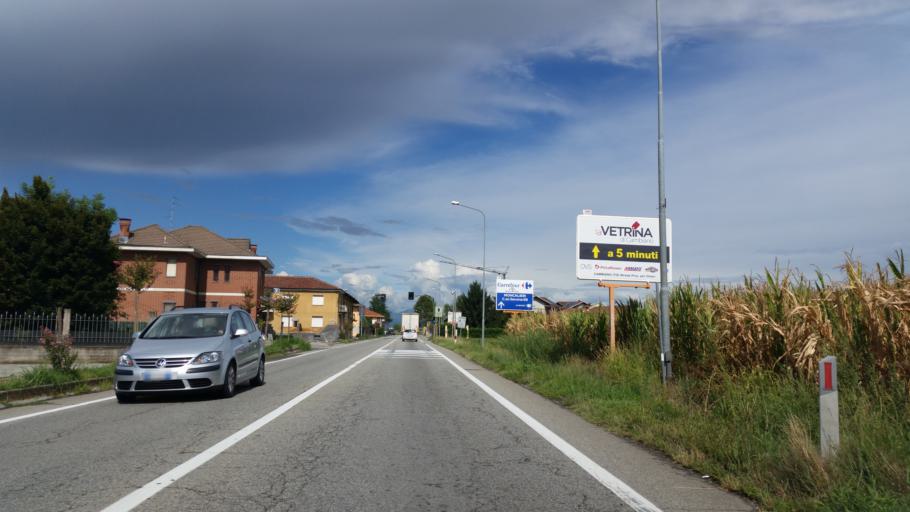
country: IT
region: Piedmont
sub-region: Provincia di Torino
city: Marocchi
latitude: 44.9424
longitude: 7.8162
